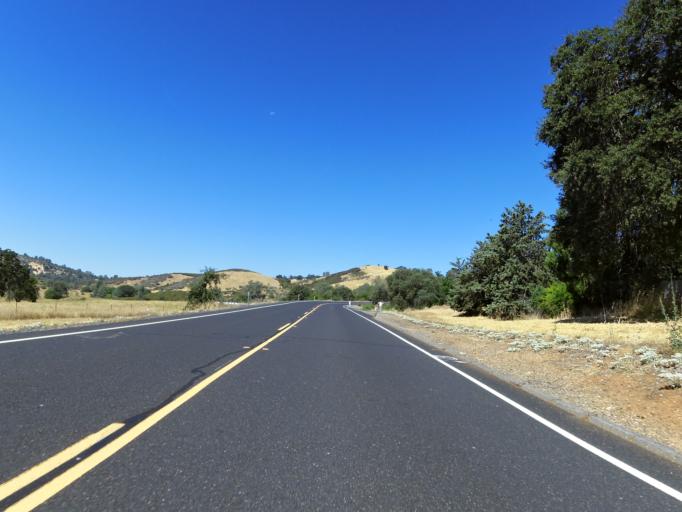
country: US
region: California
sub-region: Tuolumne County
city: Tuolumne City
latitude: 37.7001
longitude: -120.2694
